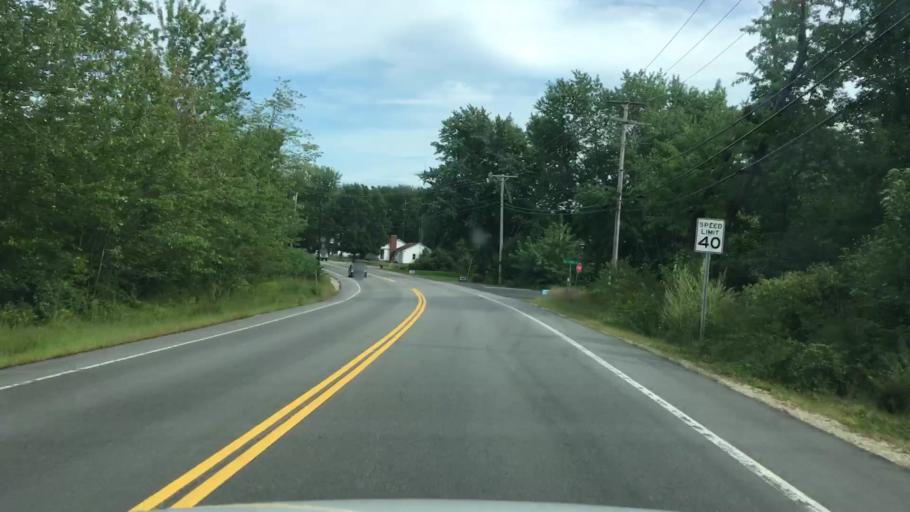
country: US
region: New Hampshire
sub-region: Strafford County
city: Madbury
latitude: 43.1895
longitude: -70.9209
